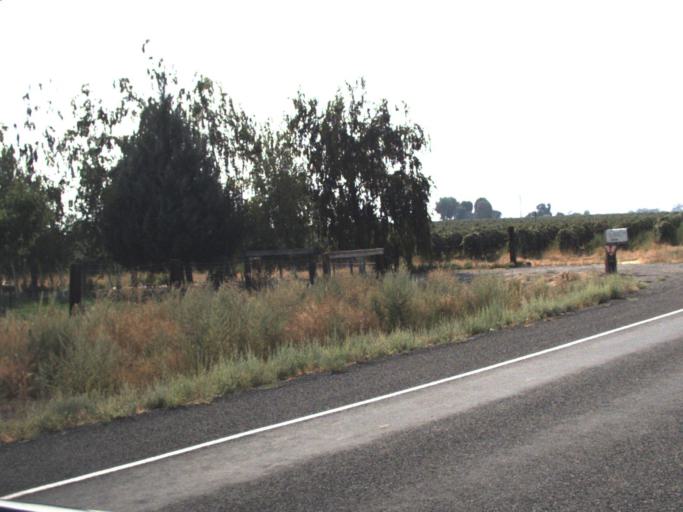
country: US
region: Washington
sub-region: Yakima County
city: Mabton
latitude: 46.2052
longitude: -119.9733
